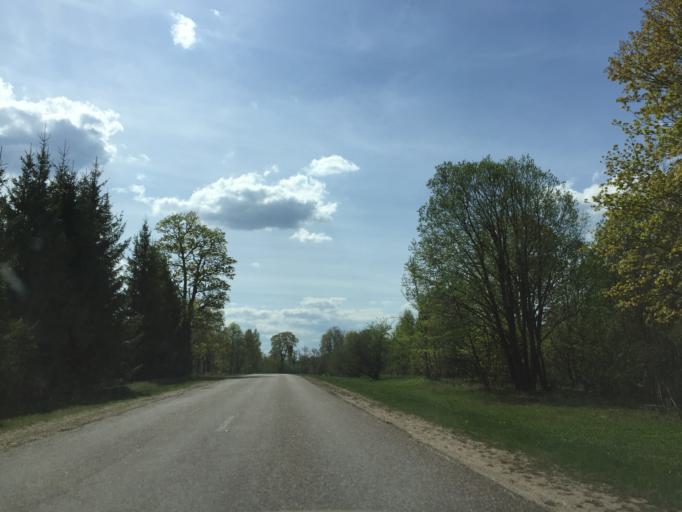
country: LV
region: Limbazu Rajons
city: Limbazi
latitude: 57.3508
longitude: 24.6650
